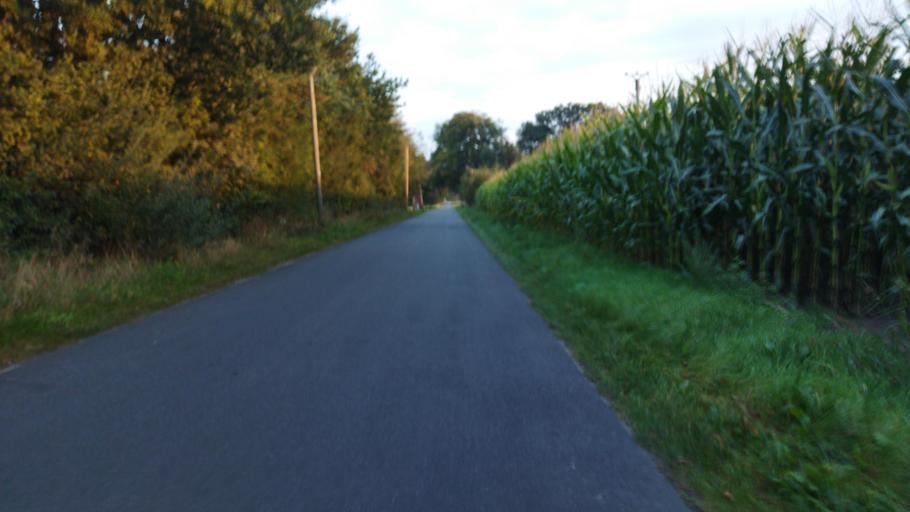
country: DE
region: Lower Saxony
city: Bad Iburg
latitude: 52.1244
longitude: 8.0575
